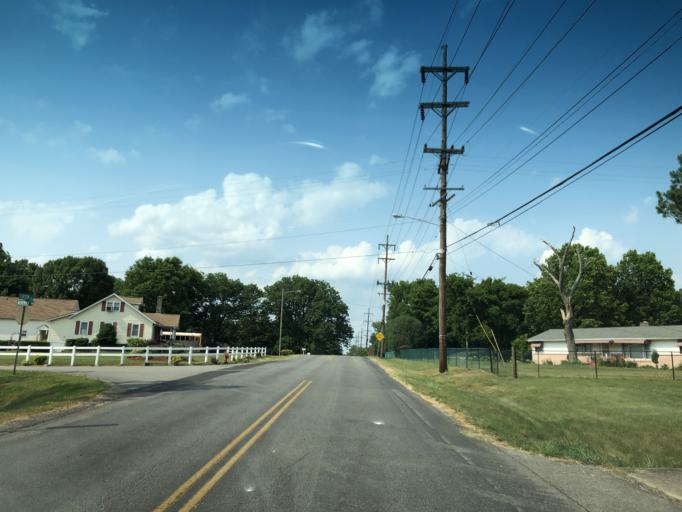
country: US
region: Tennessee
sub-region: Davidson County
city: Goodlettsville
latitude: 36.2560
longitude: -86.7202
